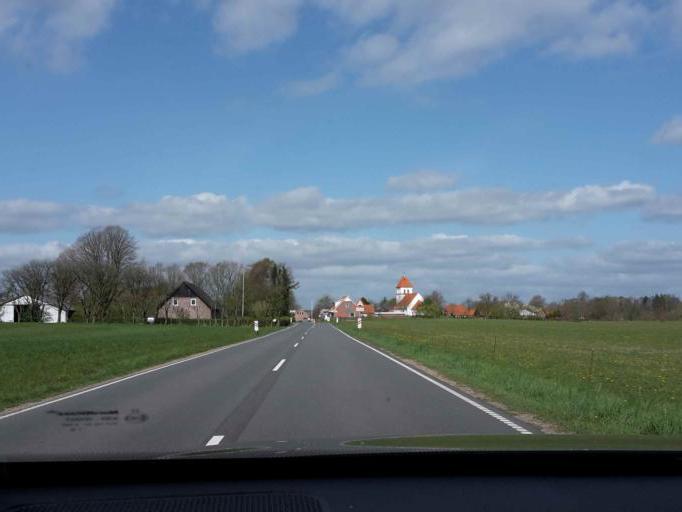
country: DK
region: South Denmark
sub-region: Billund Kommune
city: Grindsted
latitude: 55.6932
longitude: 8.8457
